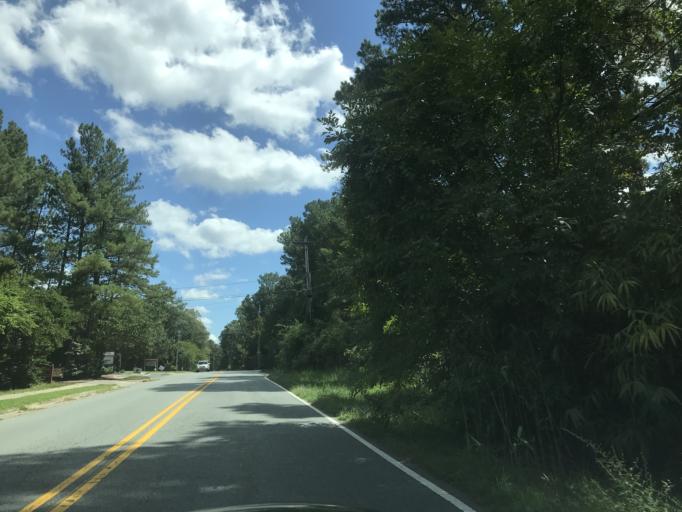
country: US
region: North Carolina
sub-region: Orange County
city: Chapel Hill
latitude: 35.9325
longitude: -79.0172
